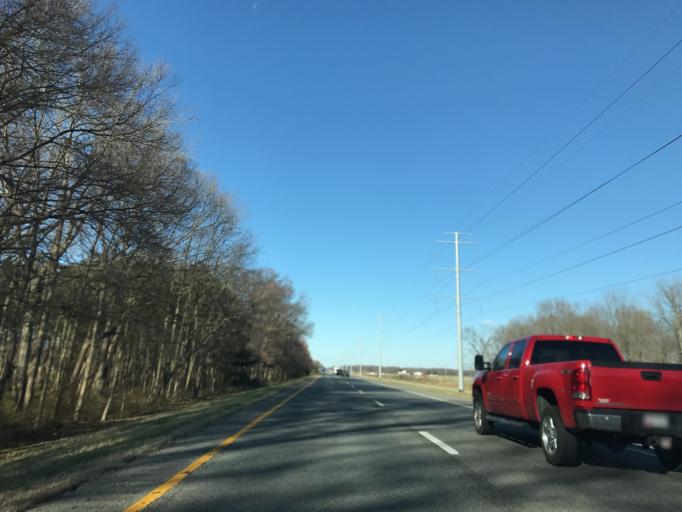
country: US
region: Maryland
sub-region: Queen Anne's County
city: Centreville
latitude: 39.0732
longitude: -75.9829
